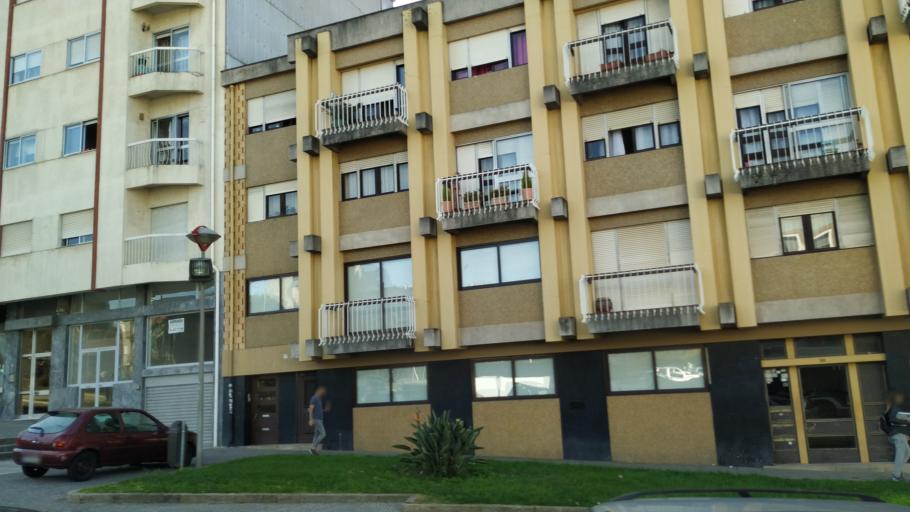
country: PT
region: Porto
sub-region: Vila Nova de Gaia
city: Vila Nova de Gaia
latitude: 41.1239
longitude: -8.6121
